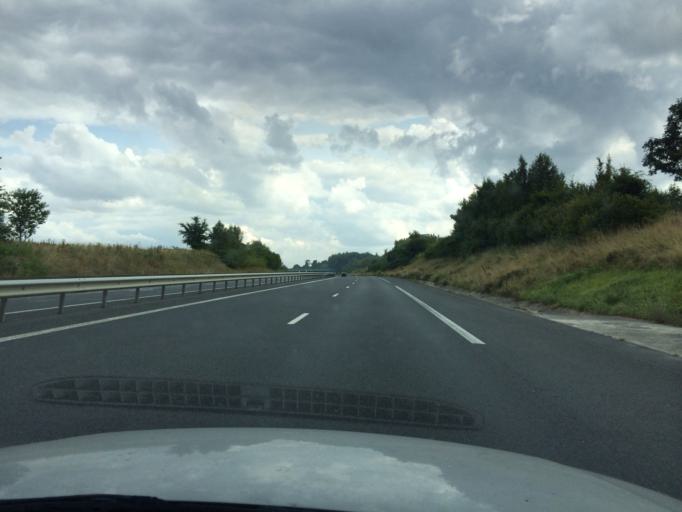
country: FR
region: Lower Normandy
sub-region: Departement du Calvados
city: Port-en-Bessin-Huppain
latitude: 49.2972
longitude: -0.7898
